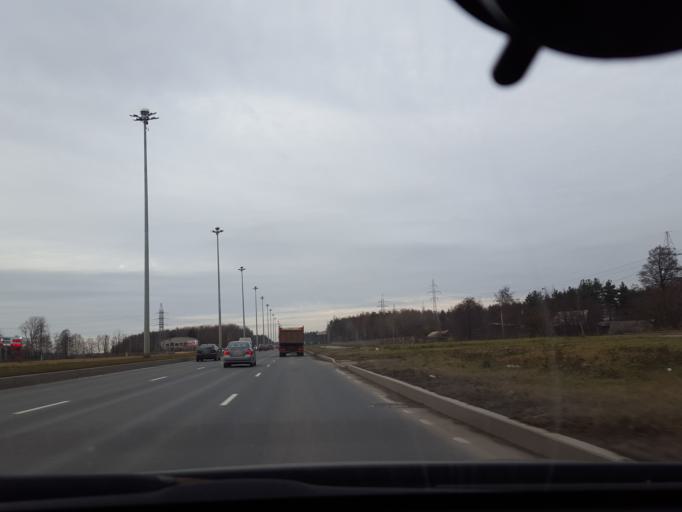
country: RU
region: Leningrad
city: Untolovo
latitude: 60.0423
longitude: 30.2394
